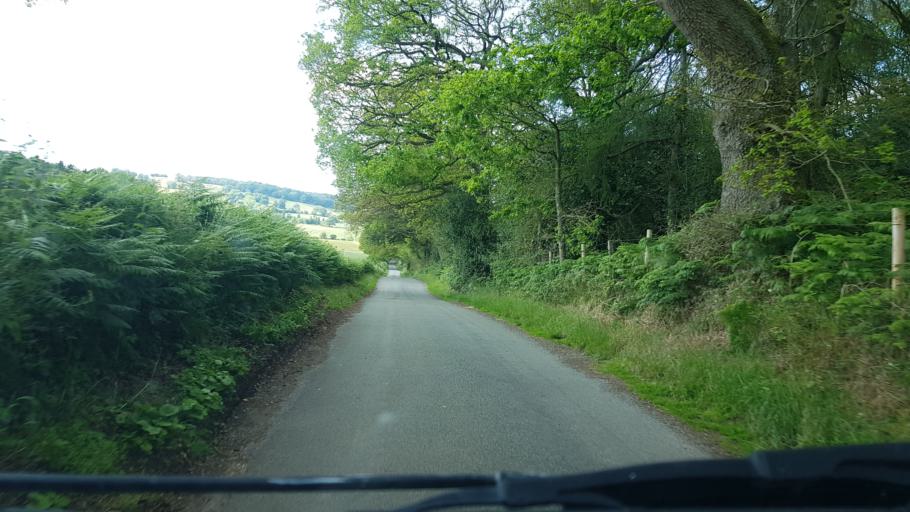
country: GB
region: England
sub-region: Worcestershire
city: Kidderminster
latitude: 52.4507
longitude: -2.2482
